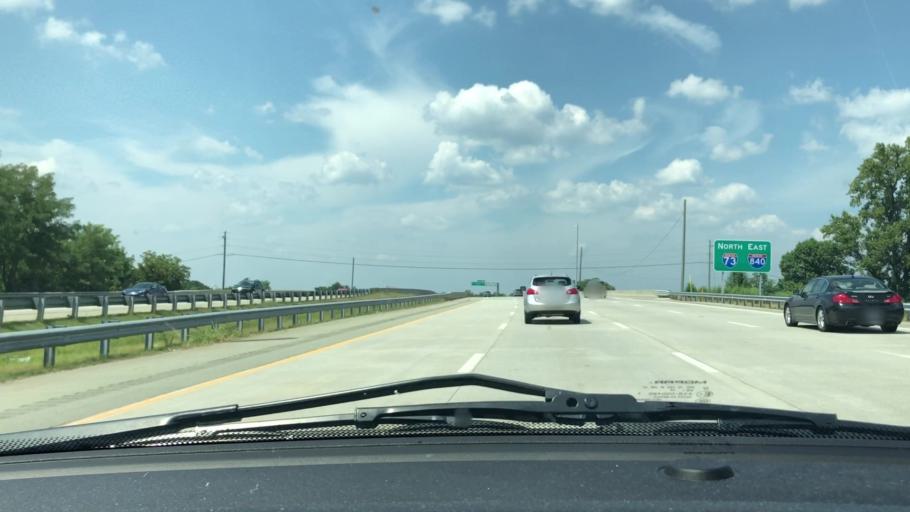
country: US
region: North Carolina
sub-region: Guilford County
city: Jamestown
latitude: 36.0744
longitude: -79.9165
